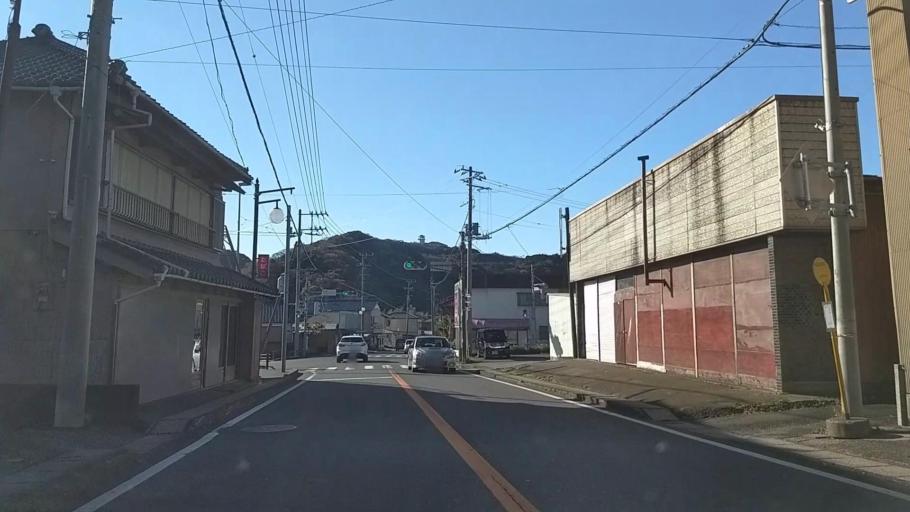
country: JP
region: Chiba
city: Futtsu
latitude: 35.2081
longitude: 139.8459
